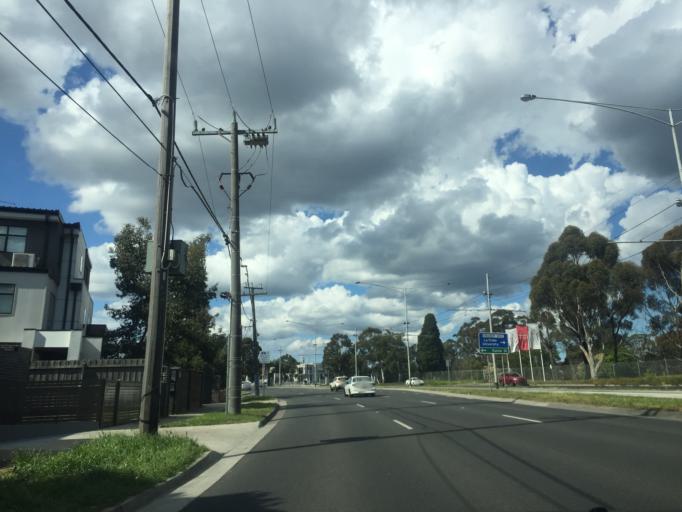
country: AU
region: Victoria
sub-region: Darebin
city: Kingsbury
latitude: -37.7181
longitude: 145.0415
